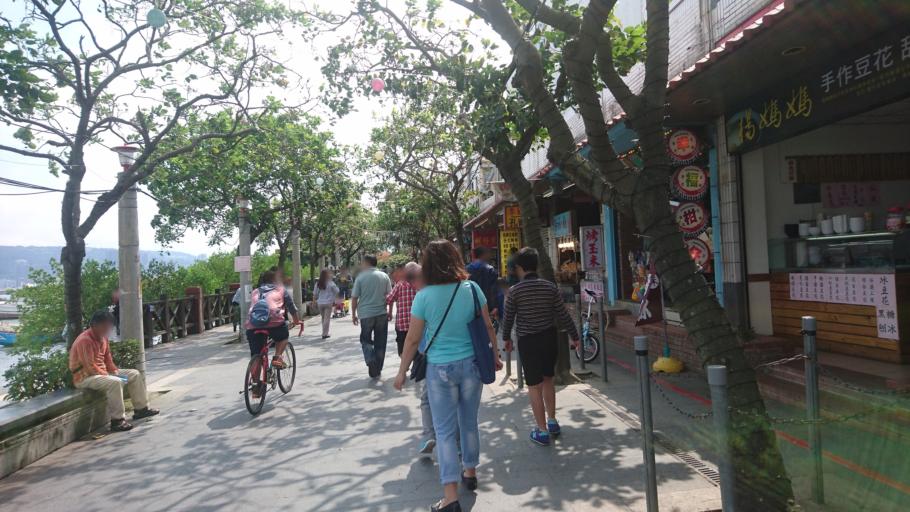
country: TW
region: Taipei
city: Taipei
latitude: 25.1594
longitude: 121.4344
